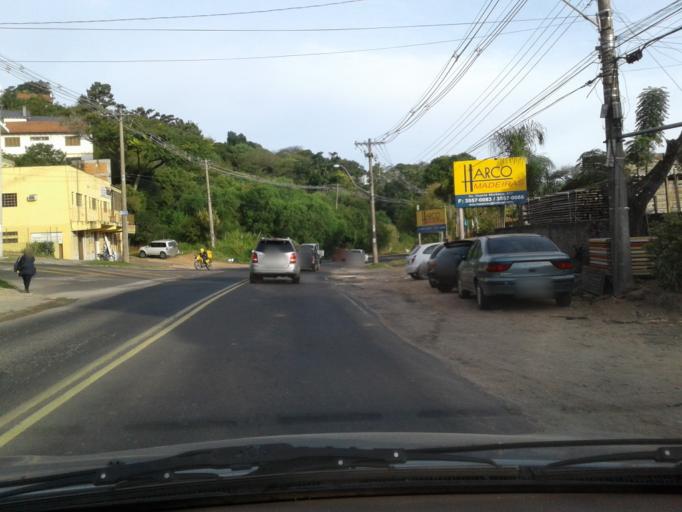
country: BR
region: Rio Grande do Sul
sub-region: Porto Alegre
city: Porto Alegre
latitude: -30.0964
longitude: -51.2250
